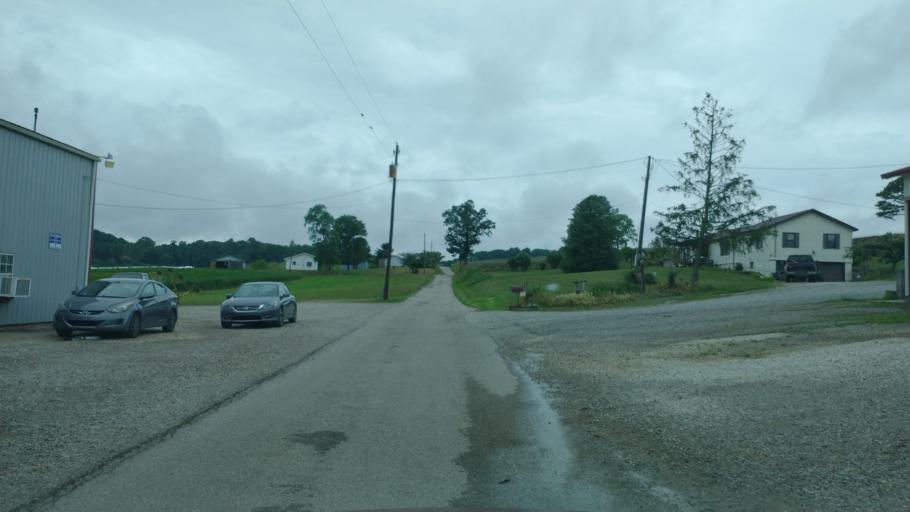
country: US
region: West Virginia
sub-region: Mason County
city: New Haven
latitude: 38.9246
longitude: -81.9706
